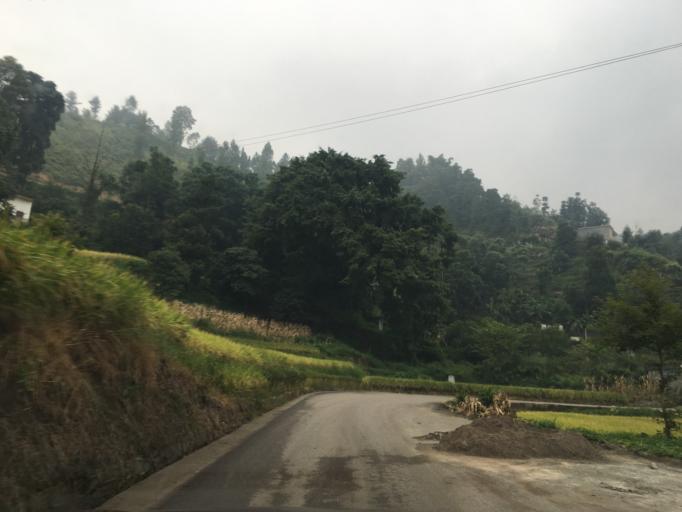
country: CN
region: Guizhou Sheng
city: Liupanshui
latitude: 26.0664
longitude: 105.1462
